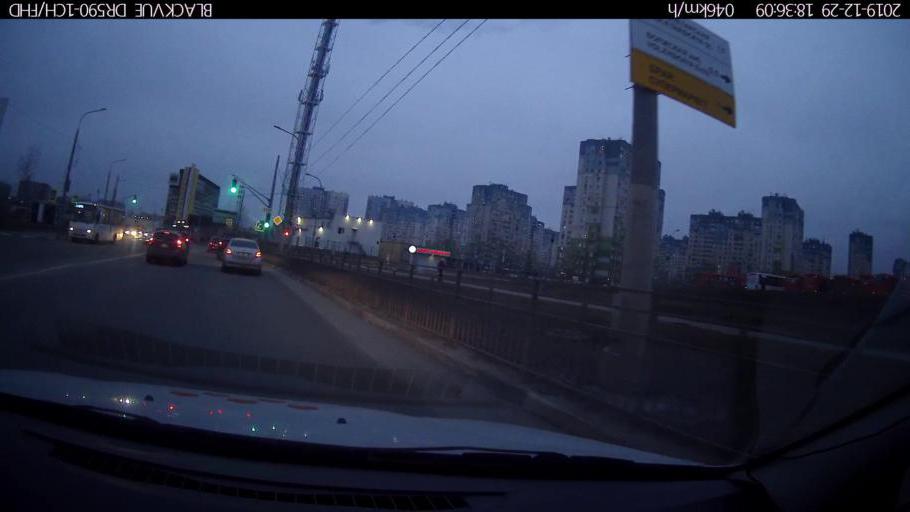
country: RU
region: Nizjnij Novgorod
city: Nizhniy Novgorod
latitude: 56.3385
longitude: 43.9522
